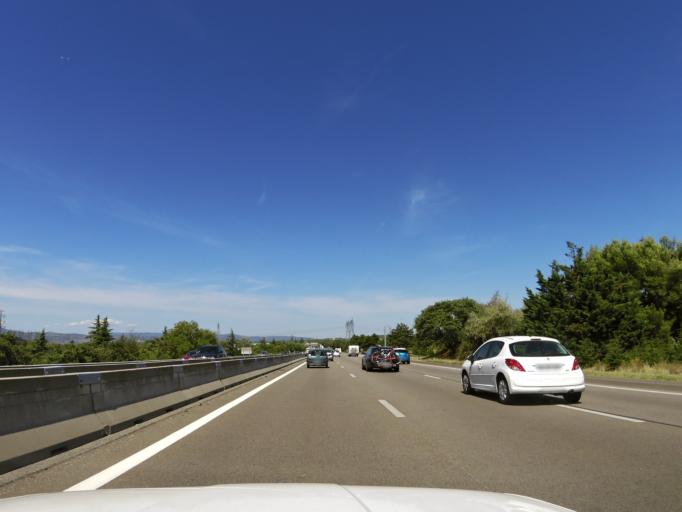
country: FR
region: Rhone-Alpes
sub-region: Departement de la Drome
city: Saulce-sur-Rhone
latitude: 44.6693
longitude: 4.7972
